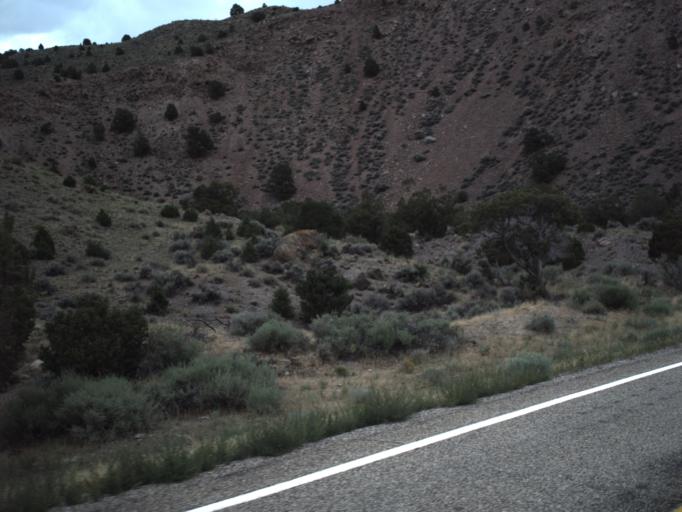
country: US
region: Utah
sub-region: Piute County
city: Junction
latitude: 38.1951
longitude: -112.1360
